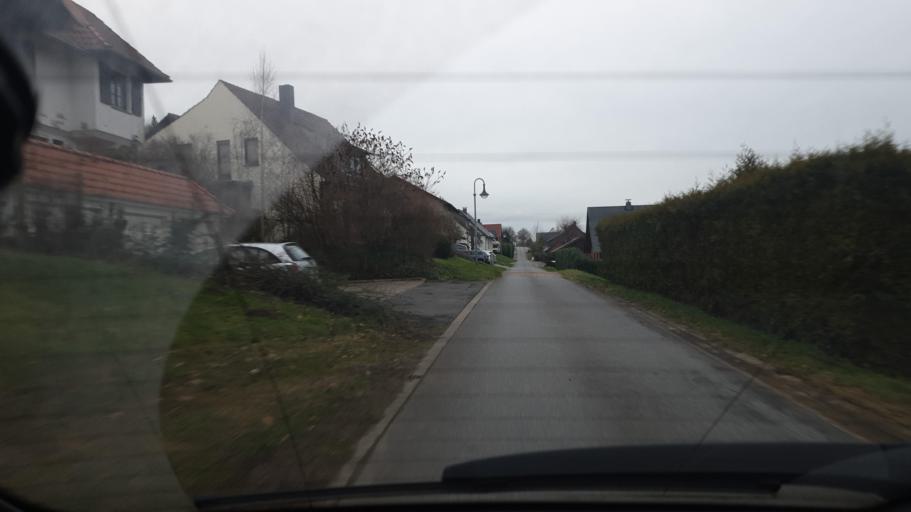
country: DE
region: North Rhine-Westphalia
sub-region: Regierungsbezirk Detmold
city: Hille
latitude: 52.2840
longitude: 8.7462
